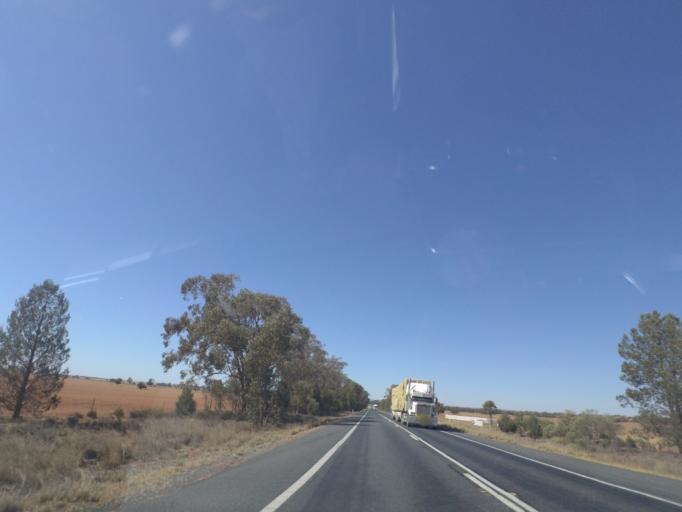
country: AU
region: New South Wales
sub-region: Bland
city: West Wyalong
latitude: -34.1820
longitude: 147.1131
